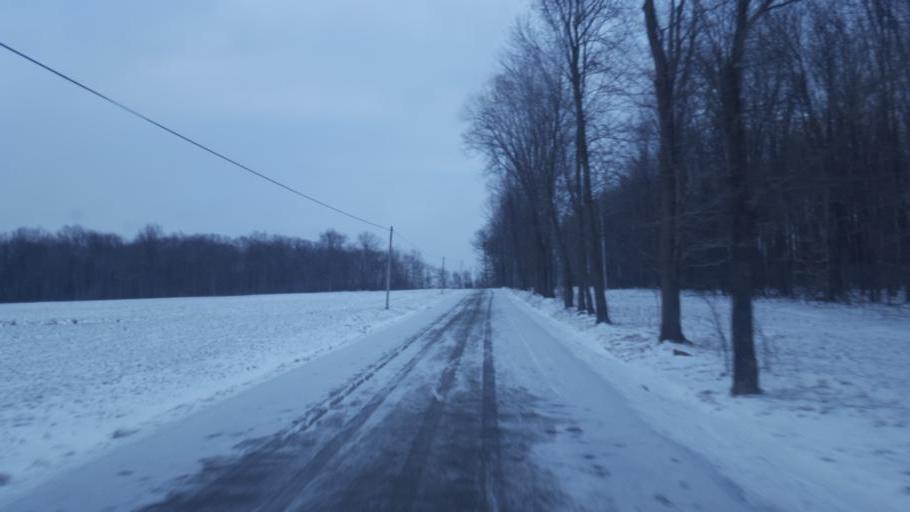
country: US
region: Pennsylvania
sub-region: Venango County
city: Sugarcreek
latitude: 41.4333
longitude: -79.9846
